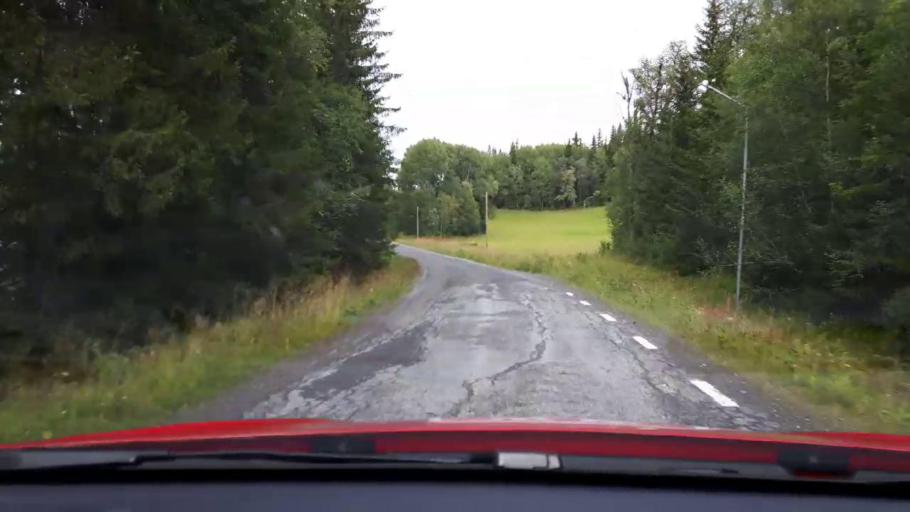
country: SE
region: Jaemtland
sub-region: Are Kommun
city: Are
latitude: 63.7472
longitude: 13.0886
